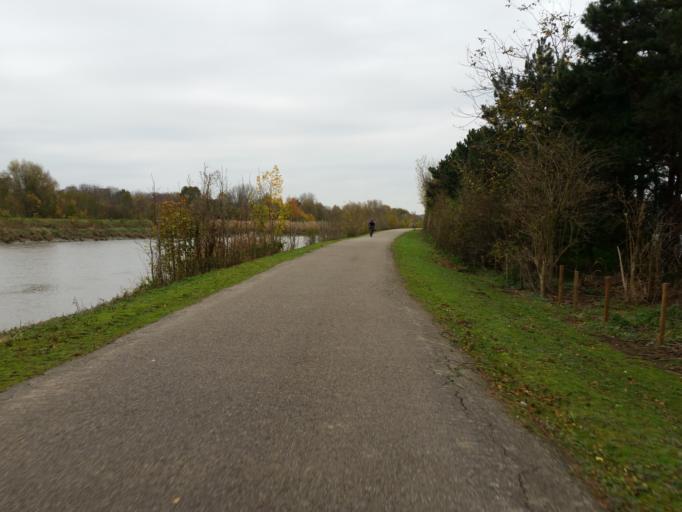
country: BE
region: Flanders
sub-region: Provincie Antwerpen
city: Duffel
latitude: 51.0884
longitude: 4.5003
